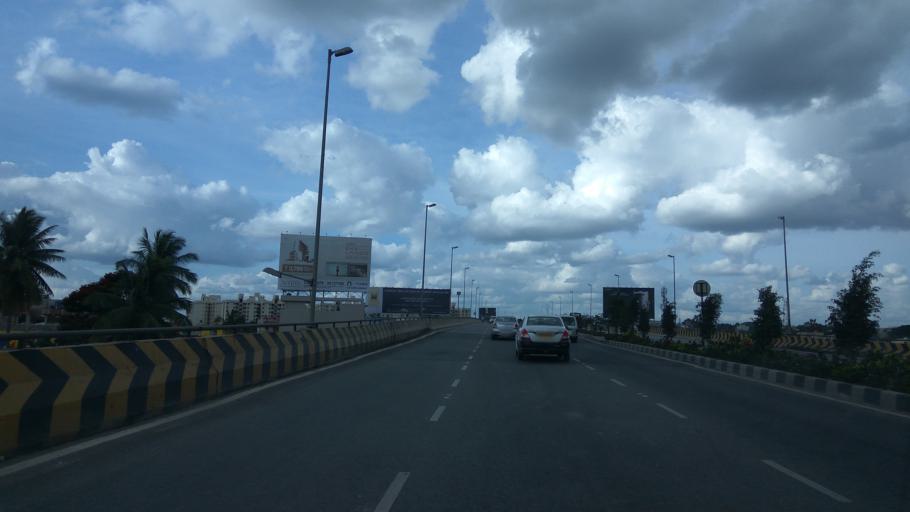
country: IN
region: Karnataka
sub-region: Bangalore Urban
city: Yelahanka
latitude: 13.1009
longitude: 77.5996
